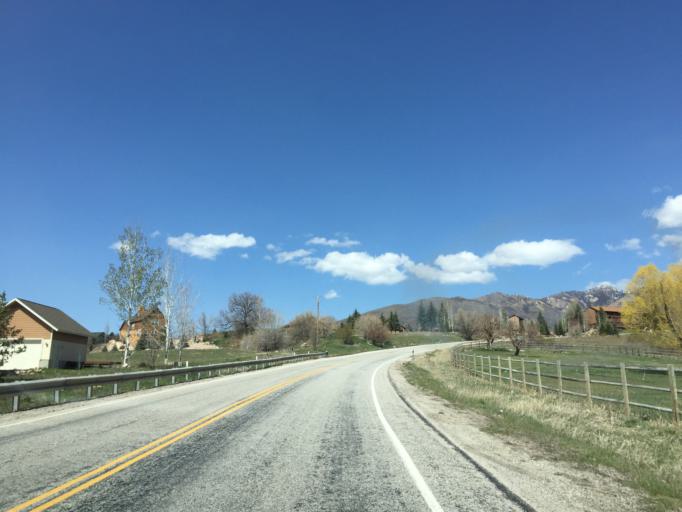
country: US
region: Utah
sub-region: Weber County
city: Wolf Creek
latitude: 41.3219
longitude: -111.8301
